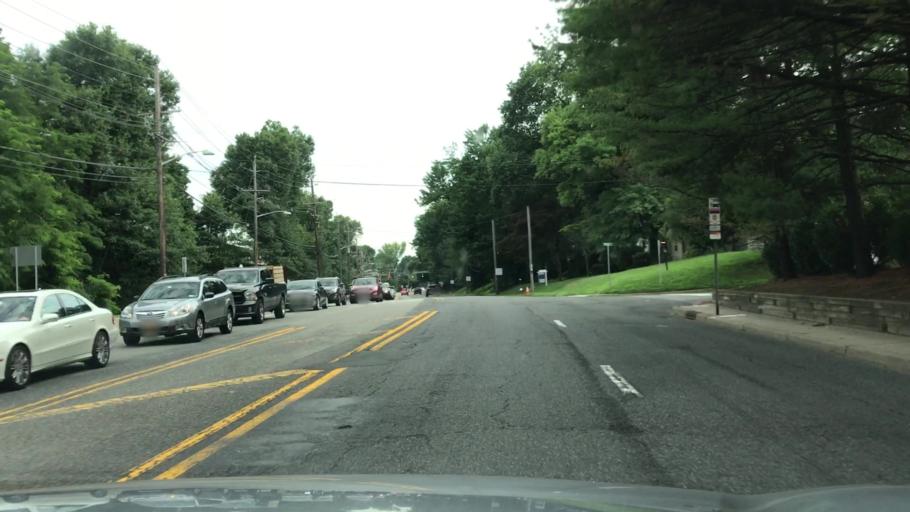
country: US
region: New Jersey
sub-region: Bergen County
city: Emerson
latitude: 40.9697
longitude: -74.0298
